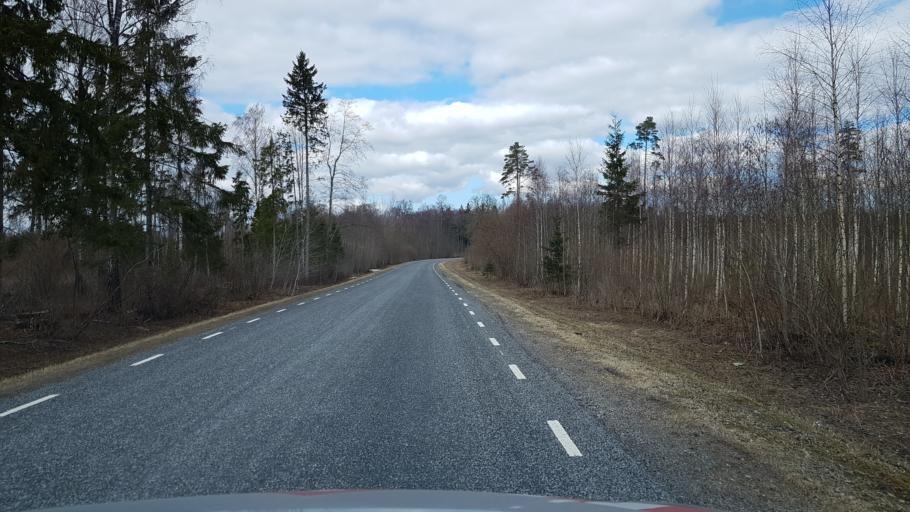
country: EE
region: Laeaene-Virumaa
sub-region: Tamsalu vald
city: Tamsalu
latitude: 59.1887
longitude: 26.1302
